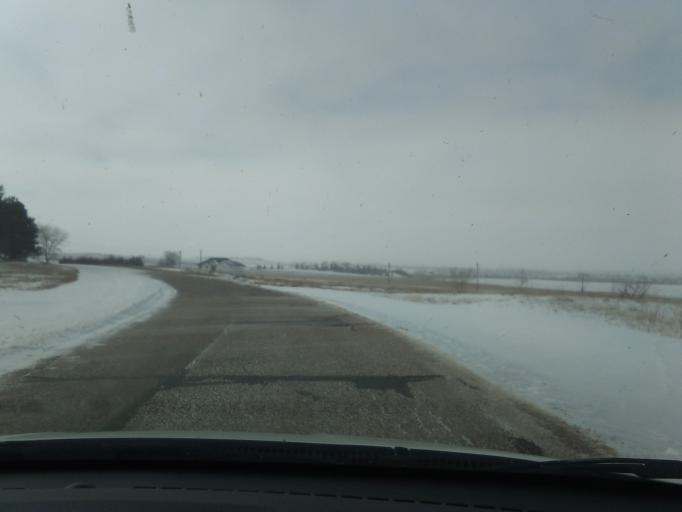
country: US
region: Nebraska
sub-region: Kimball County
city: Kimball
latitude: 41.2269
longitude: -103.6217
